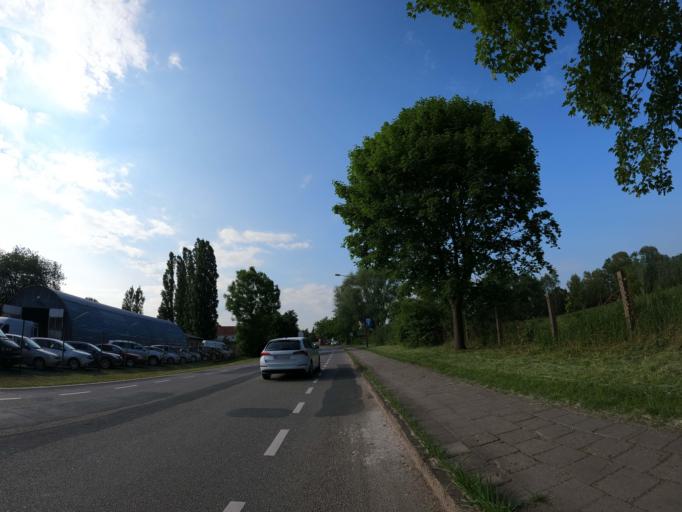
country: DE
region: Mecklenburg-Vorpommern
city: Stralsund
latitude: 54.3009
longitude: 13.0752
